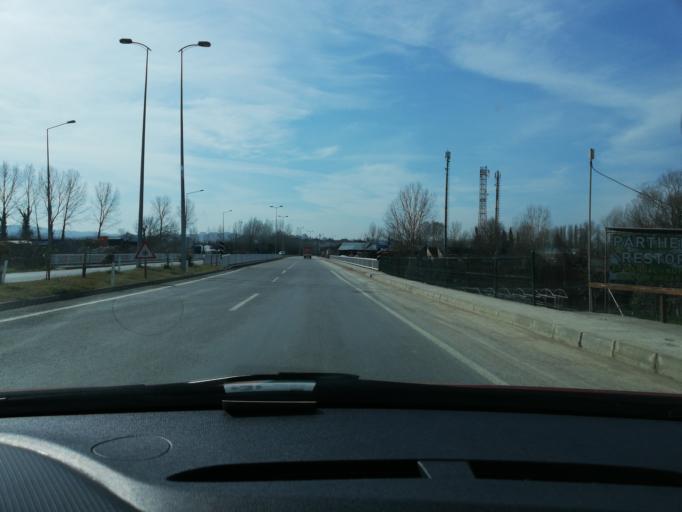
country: TR
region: Bartin
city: Bartin
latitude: 41.6420
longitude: 32.3556
